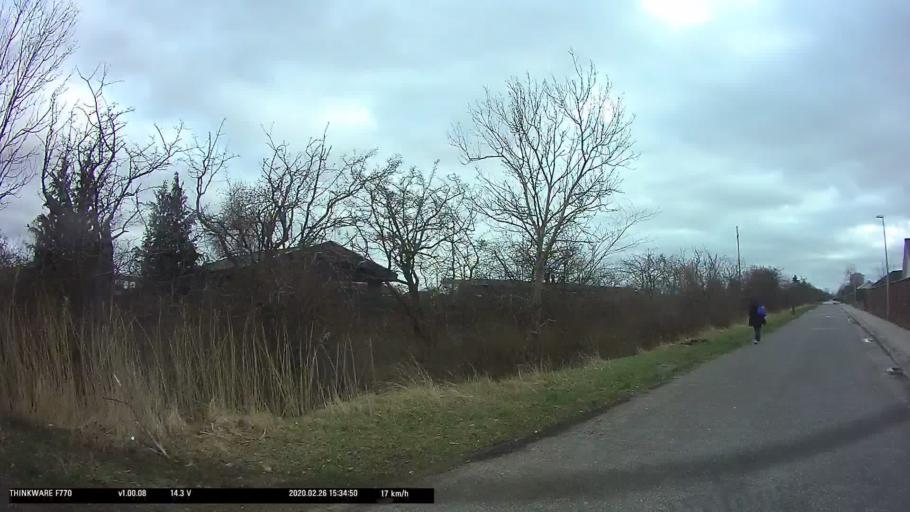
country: DK
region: Capital Region
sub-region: Tarnby Kommune
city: Tarnby
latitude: 55.6002
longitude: 12.5869
